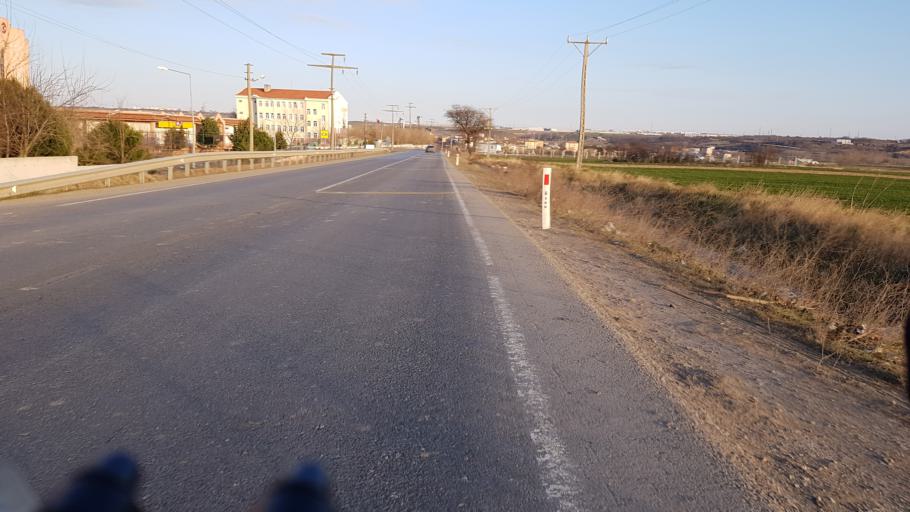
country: TR
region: Tekirdag
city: Velimese
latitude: 41.2522
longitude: 27.8663
